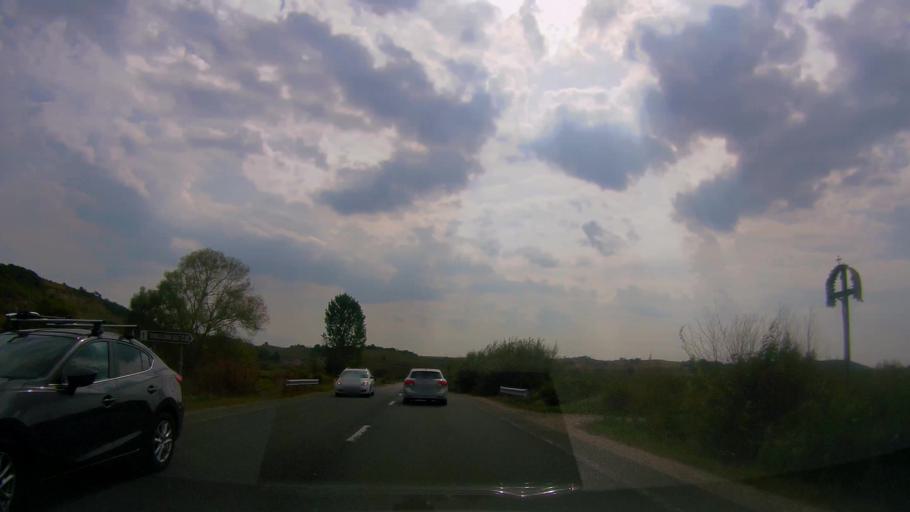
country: RO
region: Cluj
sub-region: Comuna Sanpaul
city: Sanpaul
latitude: 46.8844
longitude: 23.4169
